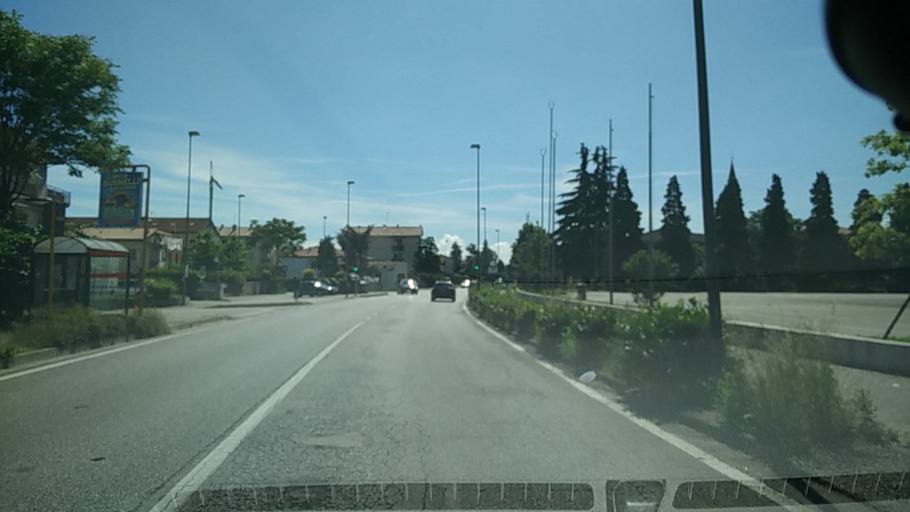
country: IT
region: Veneto
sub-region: Provincia di Venezia
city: Scorze
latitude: 45.5748
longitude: 12.1053
